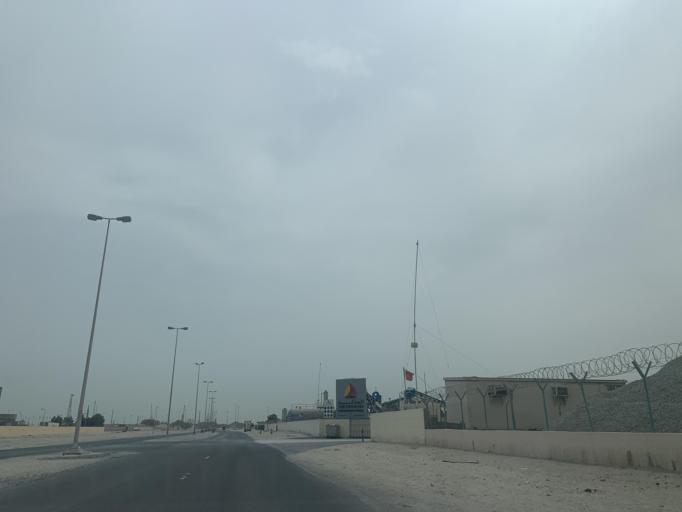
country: BH
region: Muharraq
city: Al Hadd
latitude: 26.2062
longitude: 50.6595
